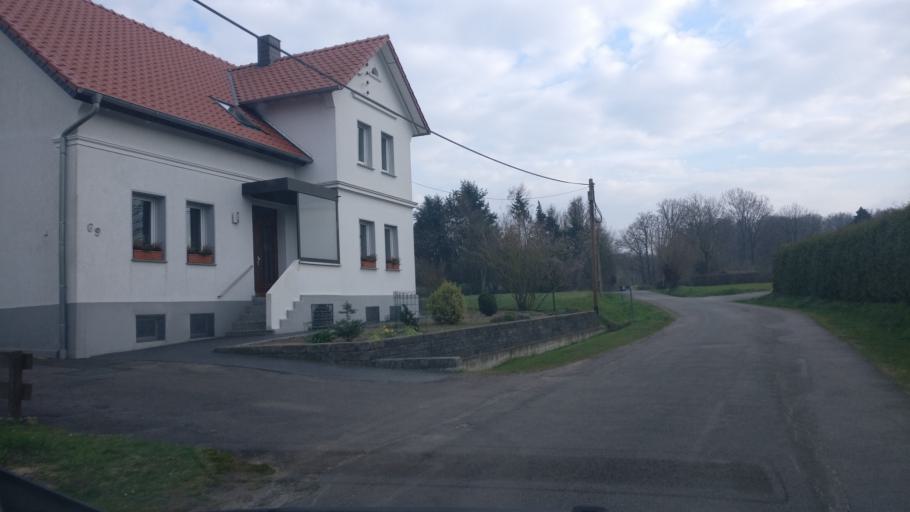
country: DE
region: North Rhine-Westphalia
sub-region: Regierungsbezirk Detmold
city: Lage
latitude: 52.0089
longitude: 8.7843
